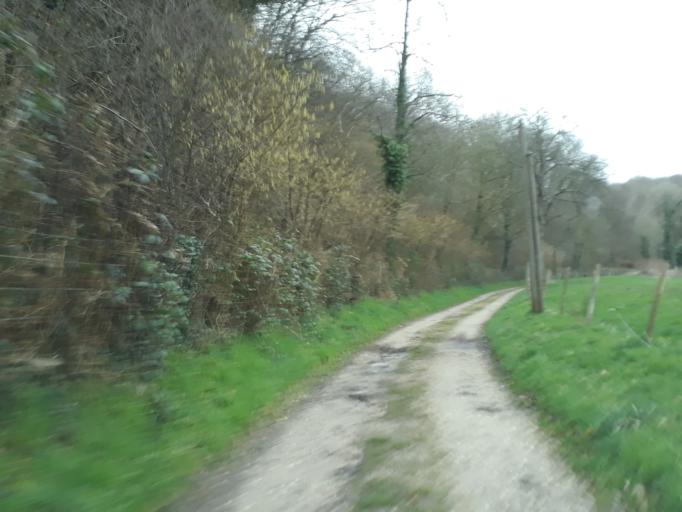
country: FR
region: Haute-Normandie
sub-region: Departement de la Seine-Maritime
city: Yport
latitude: 49.7254
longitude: 0.2971
